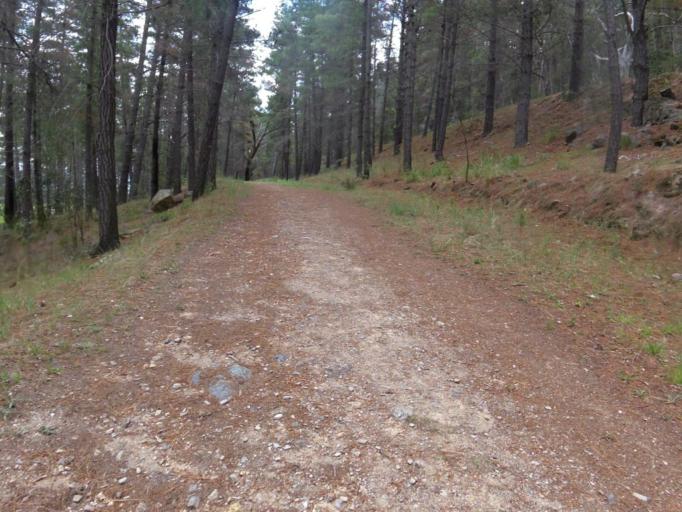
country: AU
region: Australian Capital Territory
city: Macarthur
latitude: -35.3664
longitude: 149.1148
